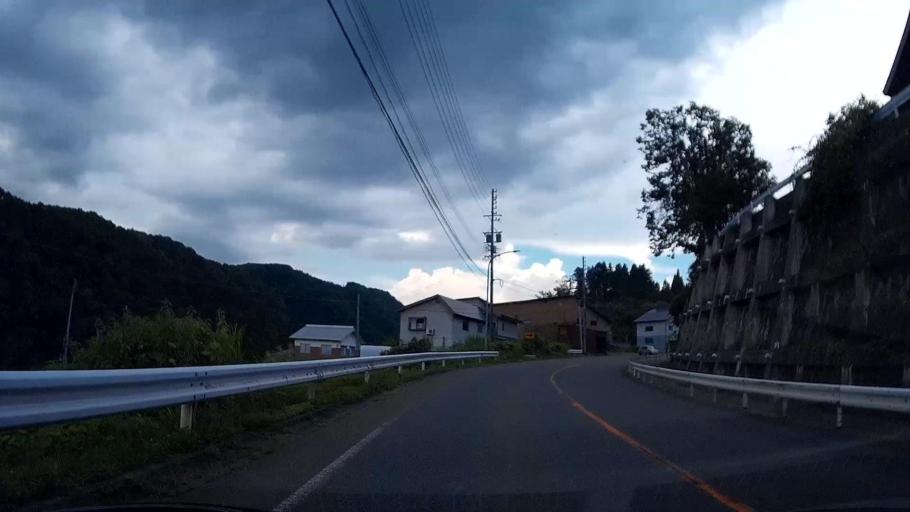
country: JP
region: Nagano
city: Iiyama
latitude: 36.9850
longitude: 138.5237
